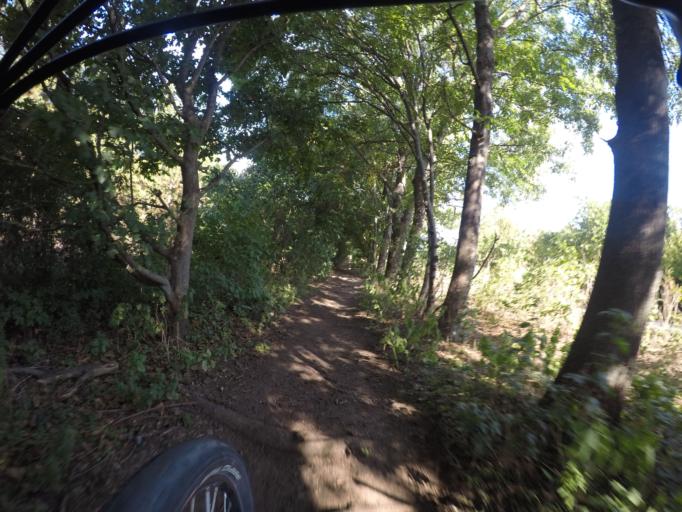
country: AT
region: Lower Austria
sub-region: Politischer Bezirk Modling
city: Modling
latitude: 48.0954
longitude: 16.3021
